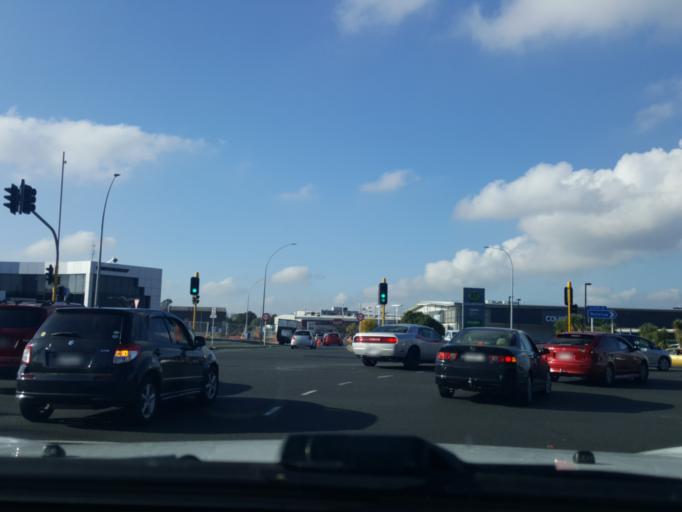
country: NZ
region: Waikato
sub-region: Hamilton City
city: Hamilton
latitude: -37.7469
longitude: 175.2327
